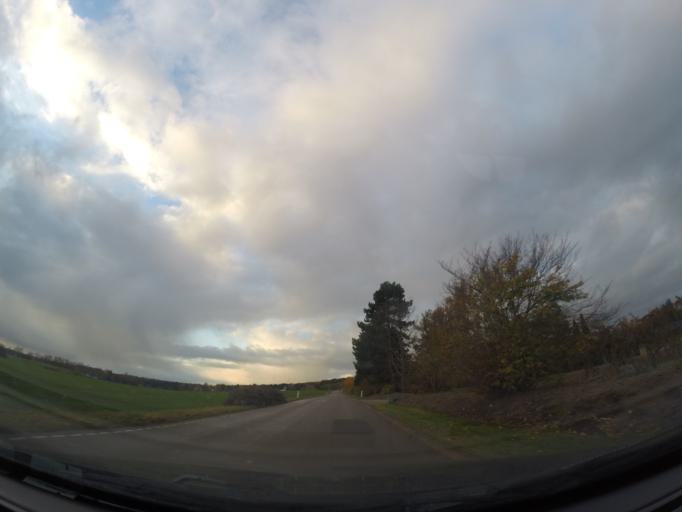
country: DK
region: Capital Region
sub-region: Hoje-Taastrup Kommune
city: Taastrup
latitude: 55.6821
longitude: 12.3063
